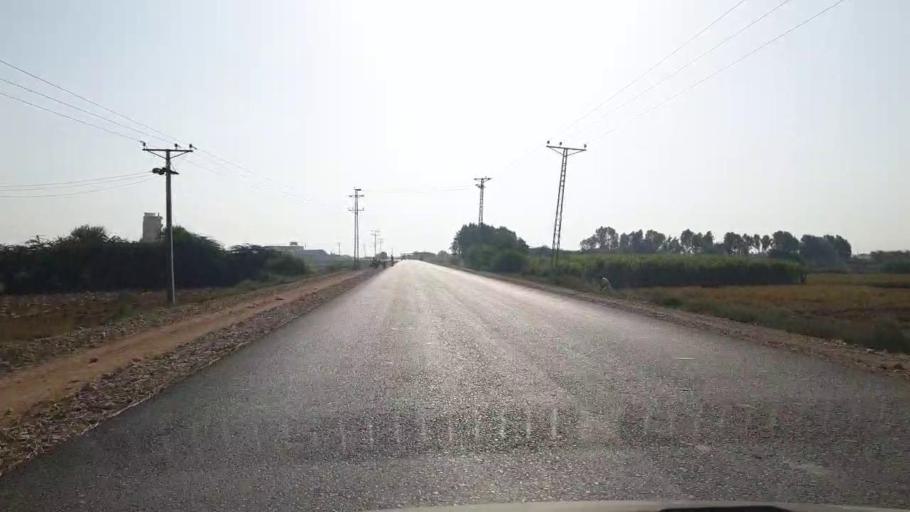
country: PK
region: Sindh
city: Badin
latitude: 24.6619
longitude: 68.8768
